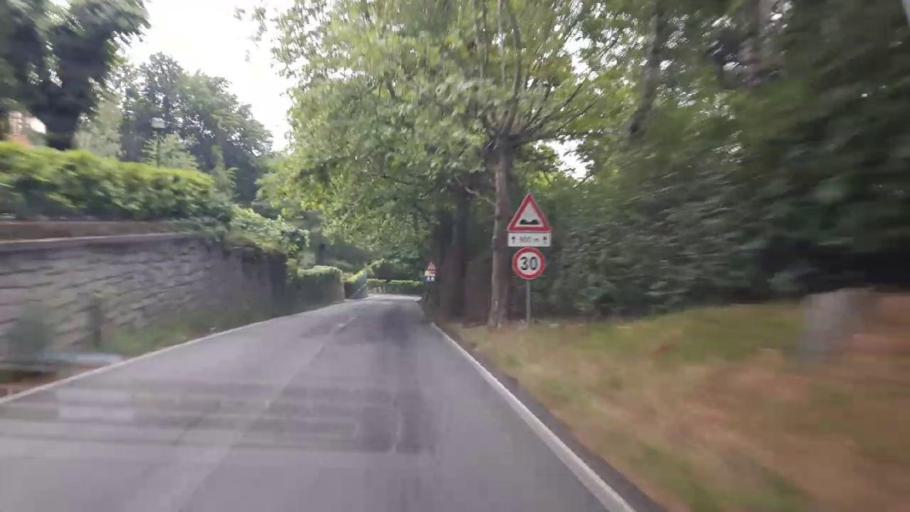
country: IT
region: Piedmont
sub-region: Provincia Verbano-Cusio-Ossola
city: Gignese
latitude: 45.8700
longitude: 8.5137
